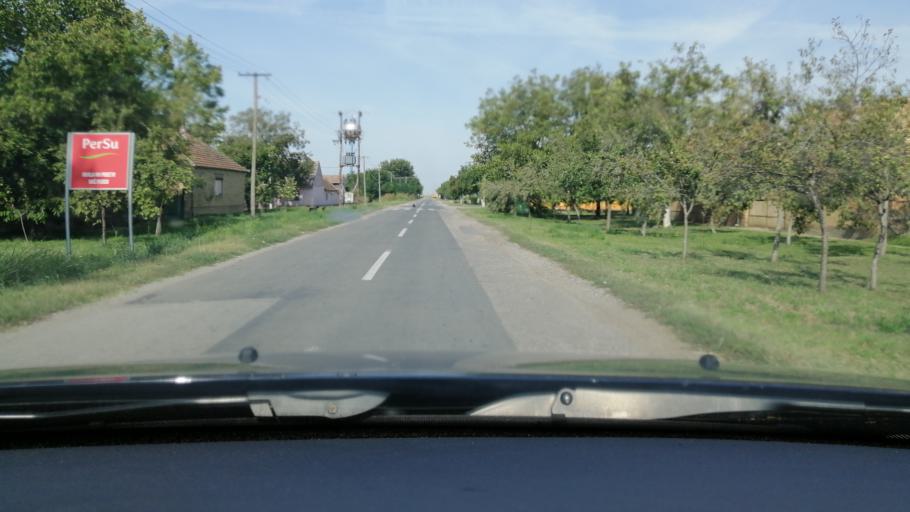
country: RS
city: Orlovat
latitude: 45.2485
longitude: 20.5820
